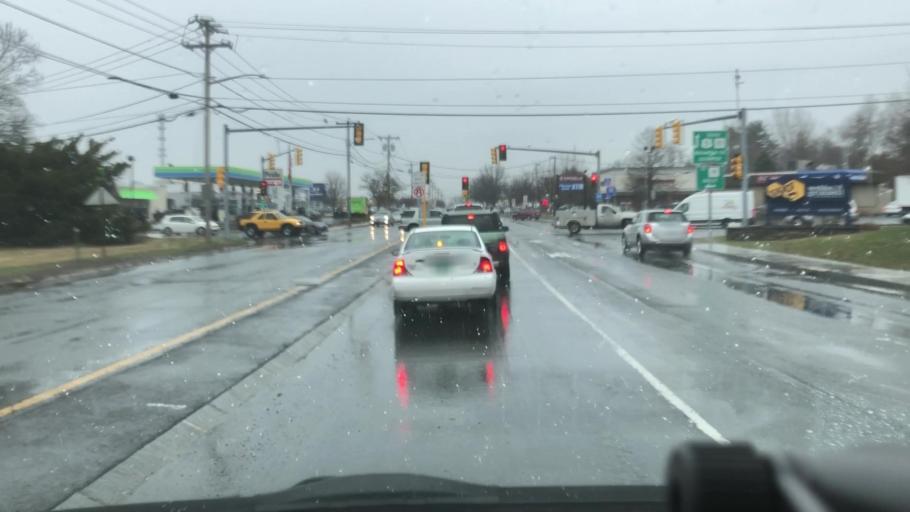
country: US
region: Massachusetts
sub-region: Hampshire County
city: Northampton
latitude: 42.3382
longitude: -72.6376
